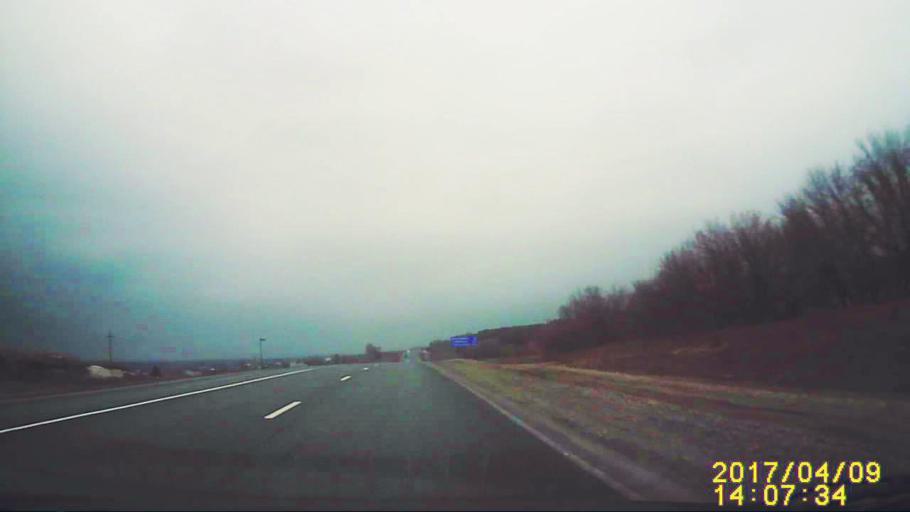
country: RU
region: Ulyanovsk
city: Silikatnyy
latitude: 54.0125
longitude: 48.2178
